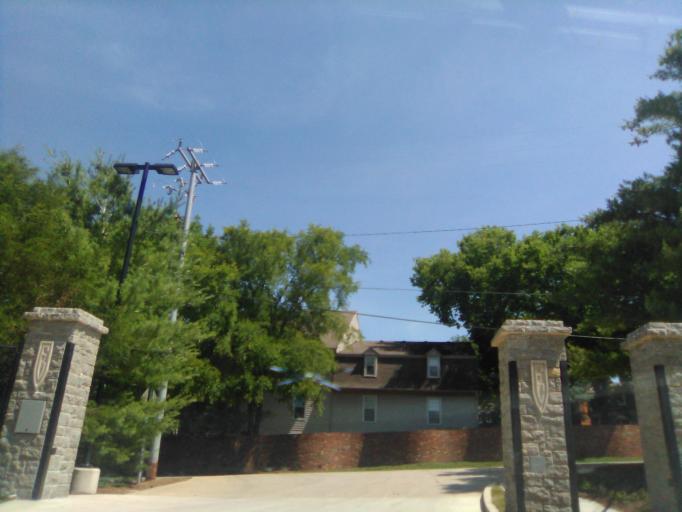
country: US
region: Tennessee
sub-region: Davidson County
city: Belle Meade
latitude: 36.1249
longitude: -86.8430
